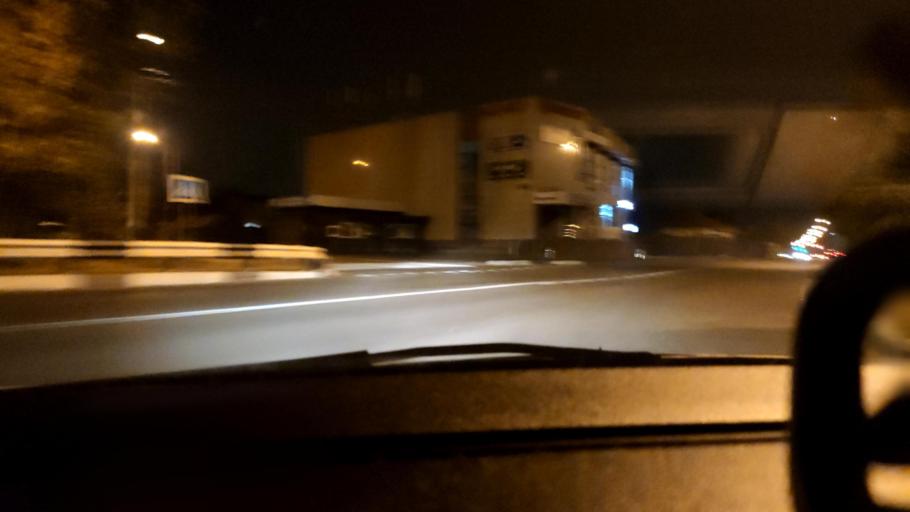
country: RU
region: Voronezj
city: Voronezh
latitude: 51.6911
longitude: 39.2088
